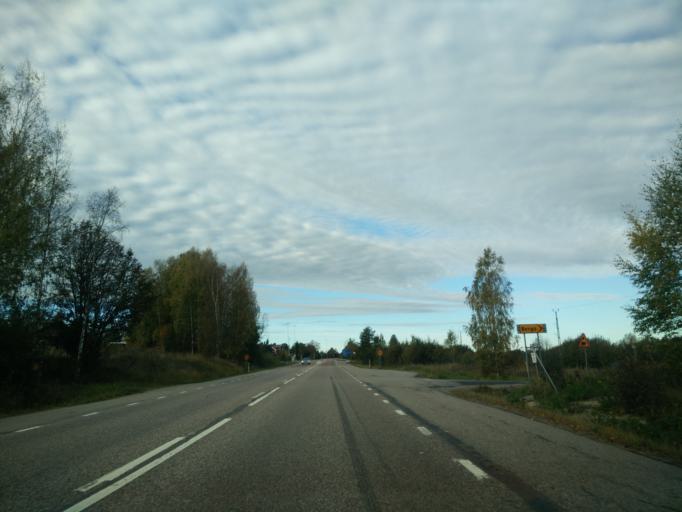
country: SE
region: Gaevleborg
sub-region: Soderhamns Kommun
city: Soderhamn
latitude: 61.2871
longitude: 16.9252
